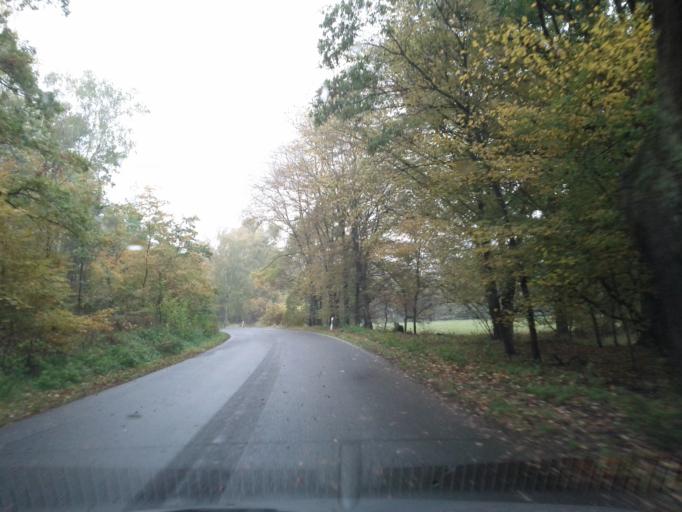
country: DE
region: Brandenburg
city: Spreenhagen
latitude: 52.3951
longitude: 13.8987
